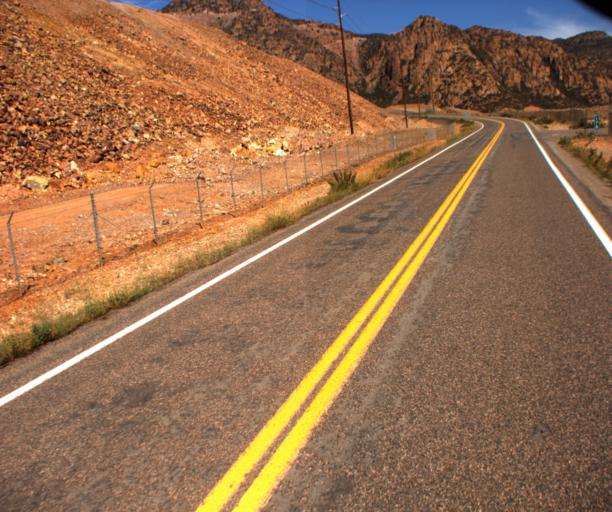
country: US
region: Arizona
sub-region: Greenlee County
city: Morenci
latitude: 33.1260
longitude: -109.3689
